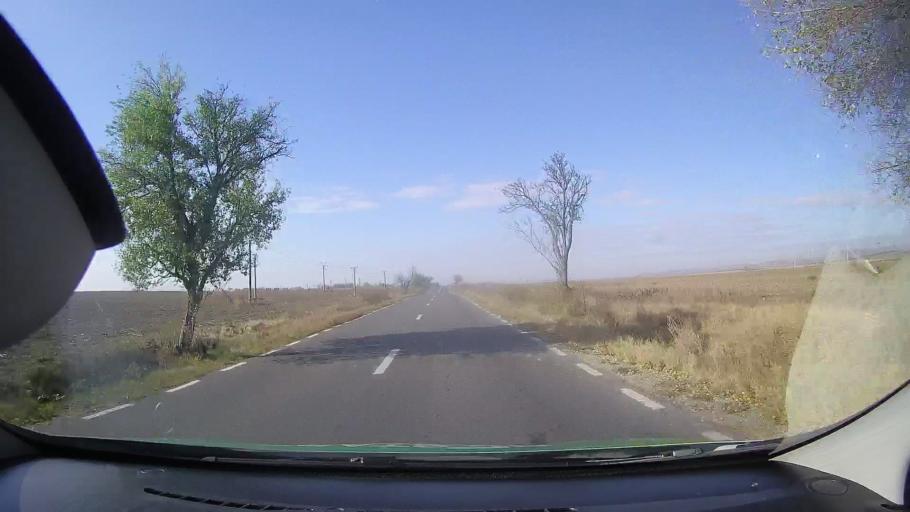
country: RO
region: Tulcea
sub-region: Comuna Murighiol
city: Murighiol
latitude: 45.0280
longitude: 29.1441
